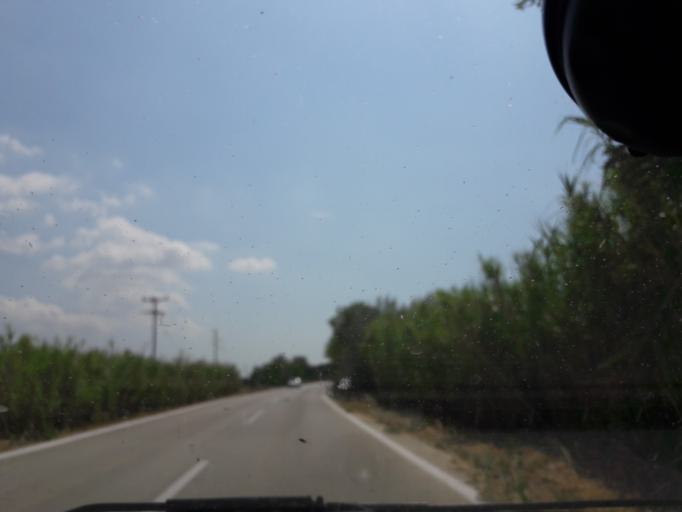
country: GR
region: North Aegean
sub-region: Nomos Lesvou
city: Myrina
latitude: 39.9332
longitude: 25.3416
